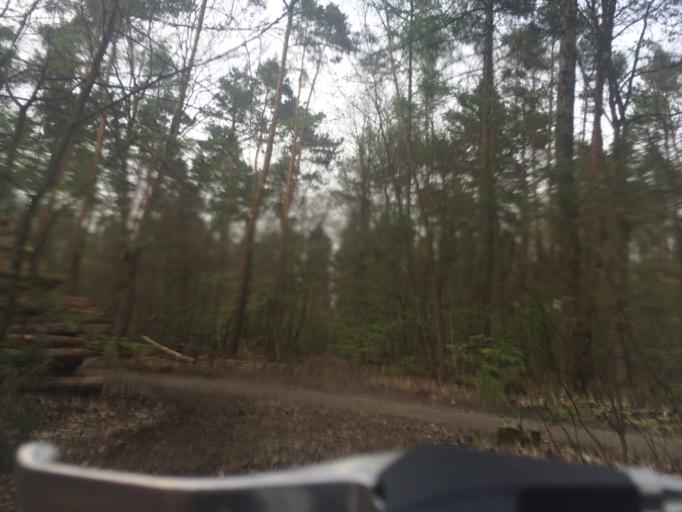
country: DE
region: Hesse
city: Morfelden-Walldorf
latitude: 50.0095
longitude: 8.5903
